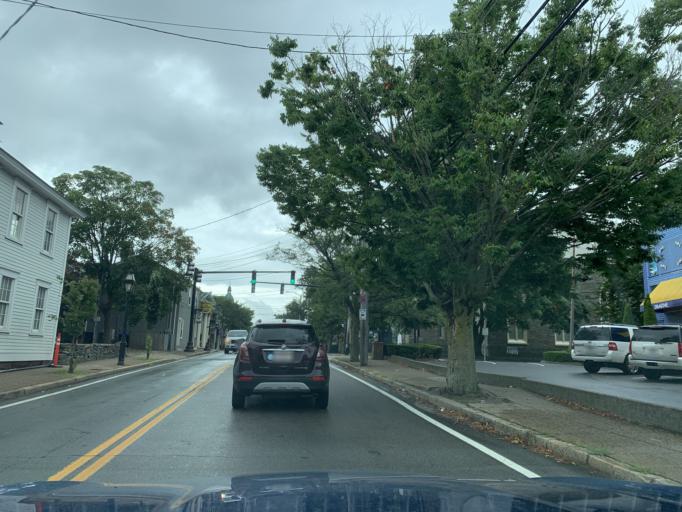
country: US
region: Rhode Island
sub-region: Bristol County
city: Warren
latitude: 41.7314
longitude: -71.2828
